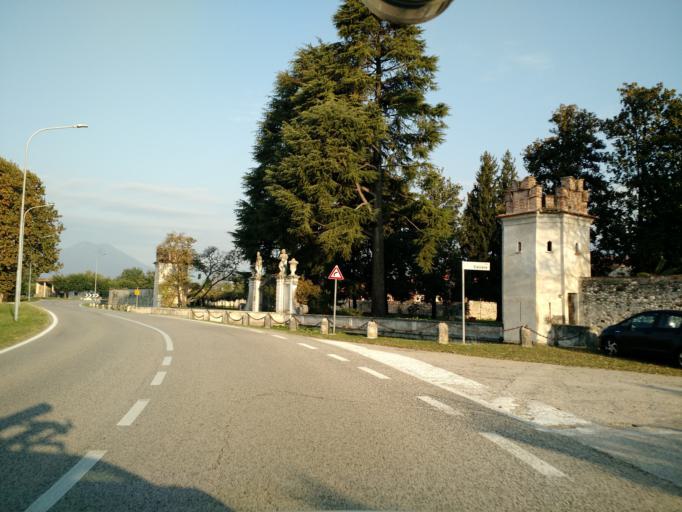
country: IT
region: Veneto
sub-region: Provincia di Vicenza
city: Sarcedo
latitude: 45.6980
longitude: 11.5387
